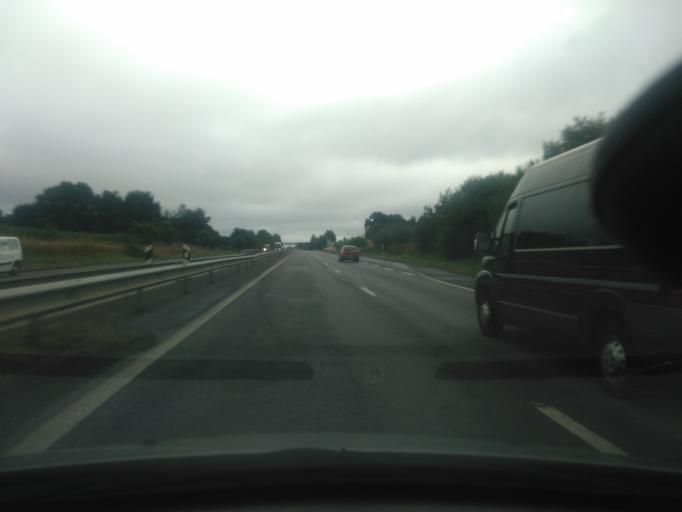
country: FR
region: Brittany
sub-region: Departement d'Ille-et-Vilaine
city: La Meziere
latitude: 48.2377
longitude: -1.7589
